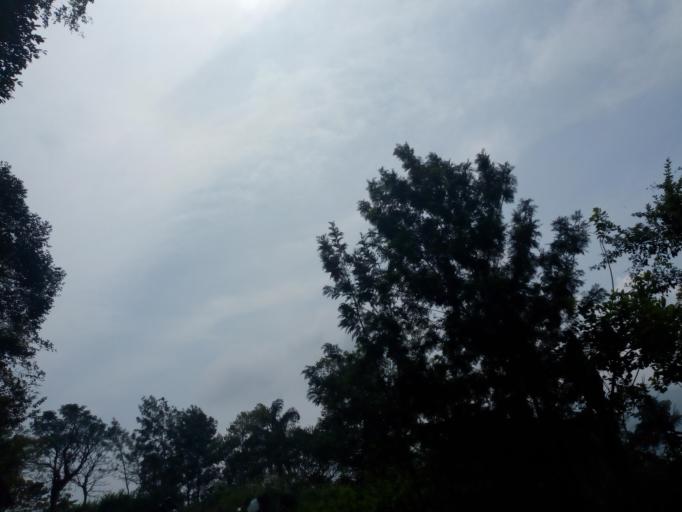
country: IN
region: Karnataka
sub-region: Dakshina Kannada
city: Sulya
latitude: 12.3806
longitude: 75.5148
